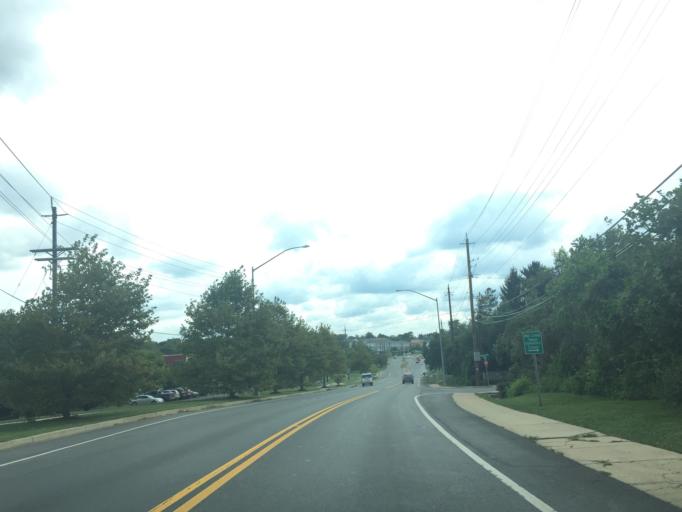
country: US
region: Maryland
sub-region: Montgomery County
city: Redland
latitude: 39.1516
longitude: -77.1503
